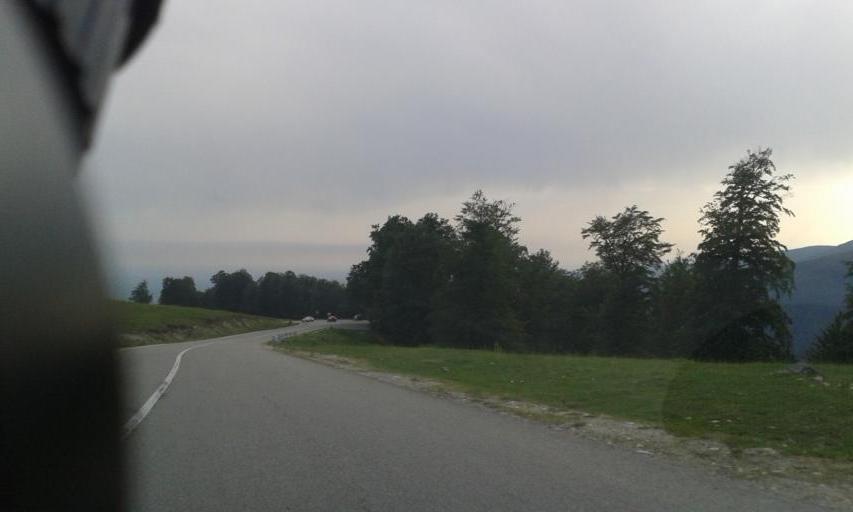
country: RO
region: Gorj
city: Novaci-Straini
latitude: 45.2386
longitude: 23.6941
